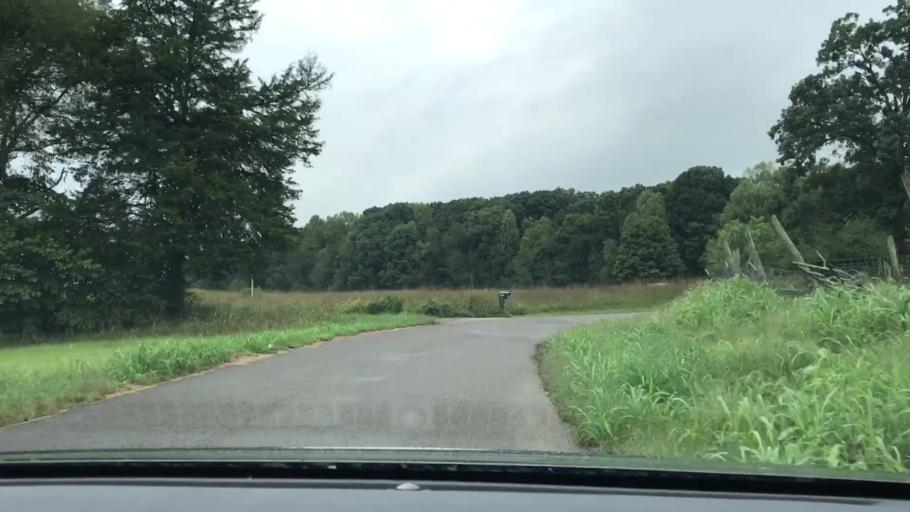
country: US
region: Kentucky
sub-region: Monroe County
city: Tompkinsville
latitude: 36.6239
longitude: -85.7724
